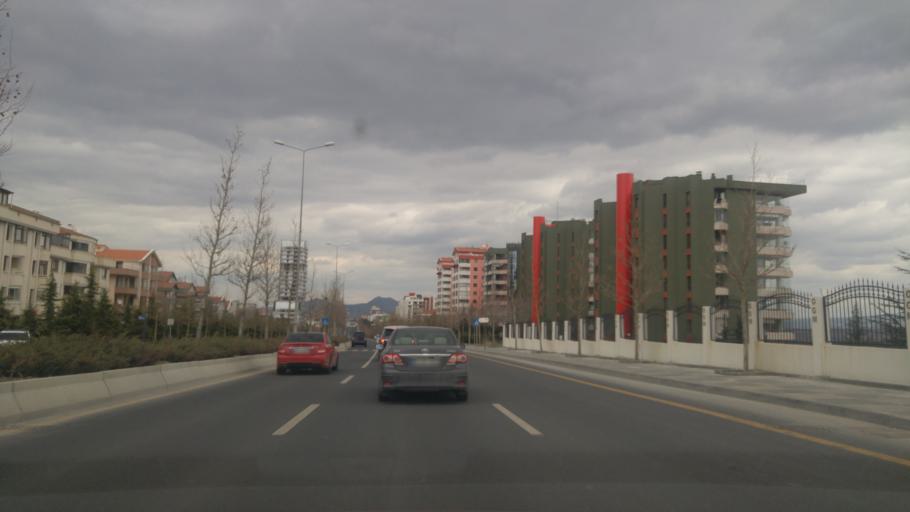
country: TR
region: Ankara
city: Cankaya
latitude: 39.8699
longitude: 32.8731
